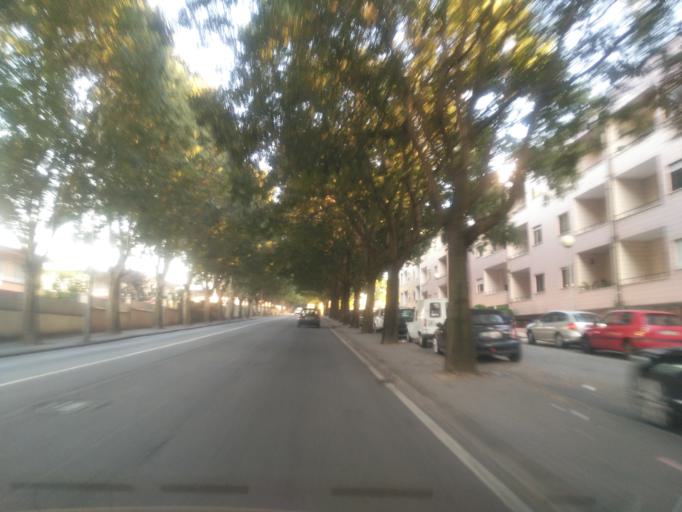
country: PT
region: Braga
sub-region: Braga
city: Braga
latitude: 41.5598
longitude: -8.4454
